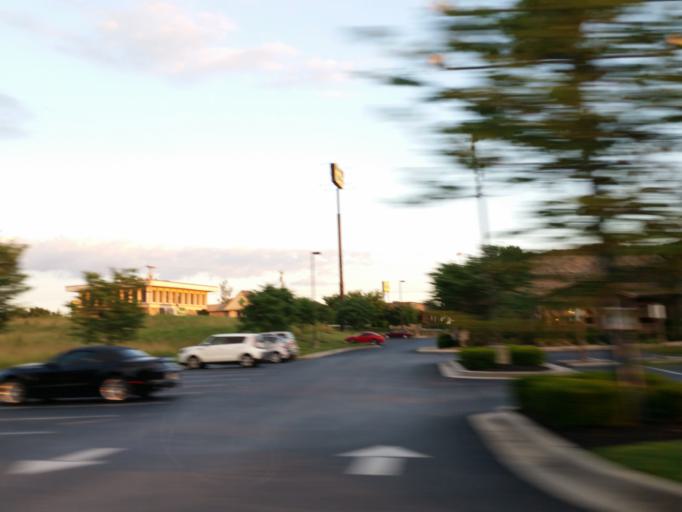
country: US
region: Tennessee
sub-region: Putnam County
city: Cookeville
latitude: 36.1380
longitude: -85.5073
